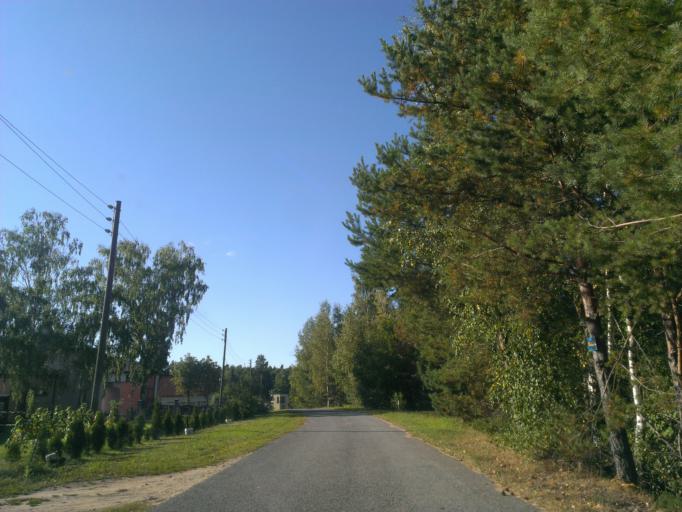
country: LV
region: Adazi
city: Adazi
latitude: 57.0667
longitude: 24.2724
